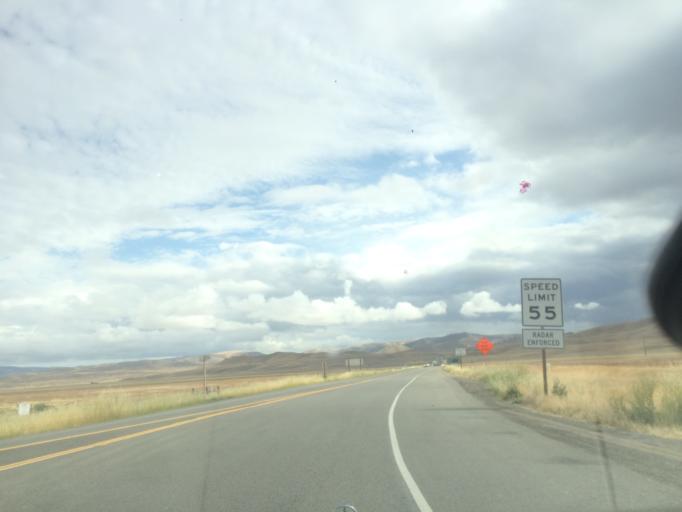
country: US
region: California
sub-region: San Luis Obispo County
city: Shandon
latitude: 35.7349
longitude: -120.2842
